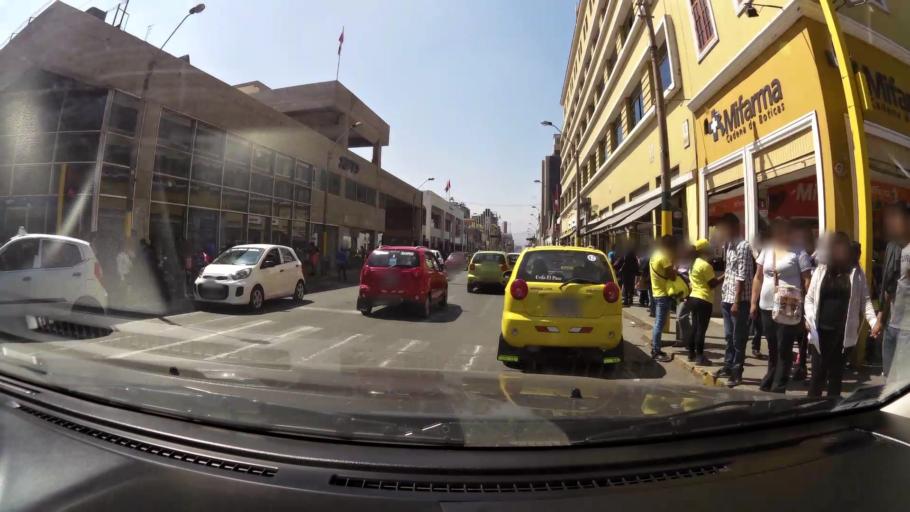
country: PE
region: Ica
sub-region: Provincia de Ica
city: Ica
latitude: -14.0634
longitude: -75.7287
